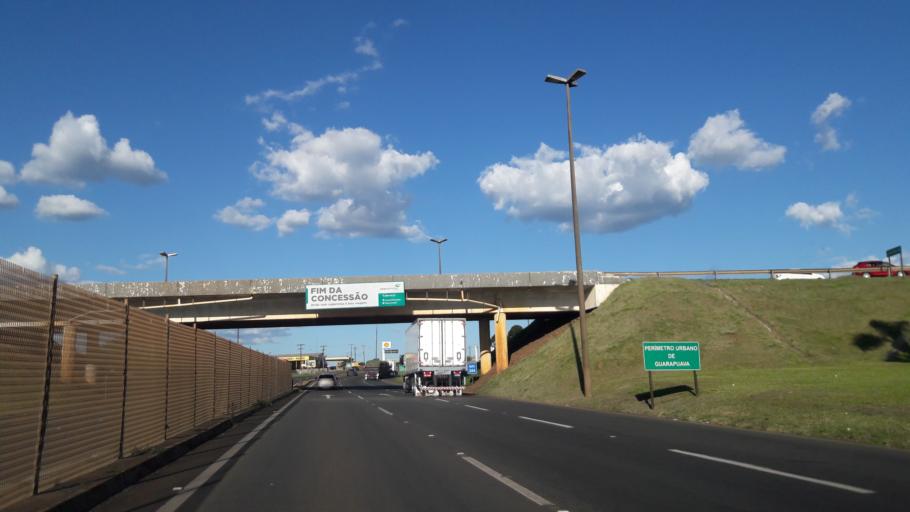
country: BR
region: Parana
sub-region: Guarapuava
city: Guarapuava
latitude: -25.3641
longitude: -51.4757
